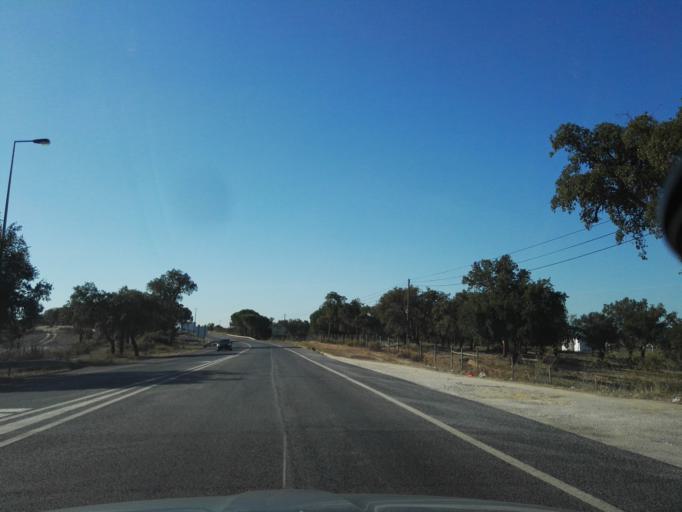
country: PT
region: Santarem
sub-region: Benavente
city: Poceirao
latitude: 38.8389
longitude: -8.7364
